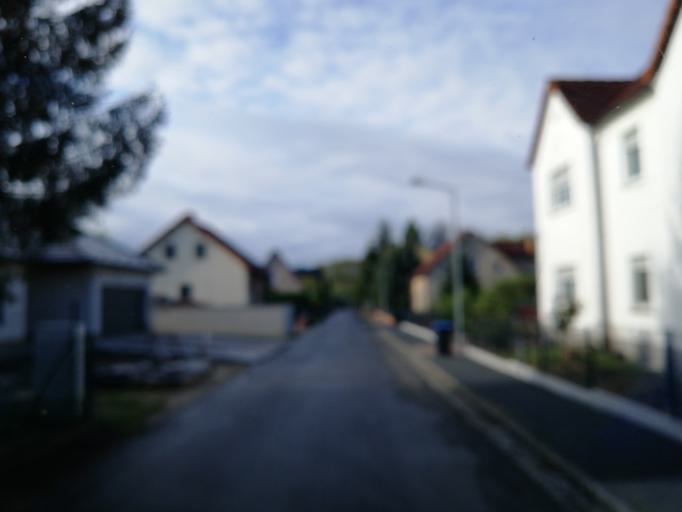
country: DE
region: Brandenburg
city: Lauchhammer
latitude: 51.4917
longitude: 13.7511
